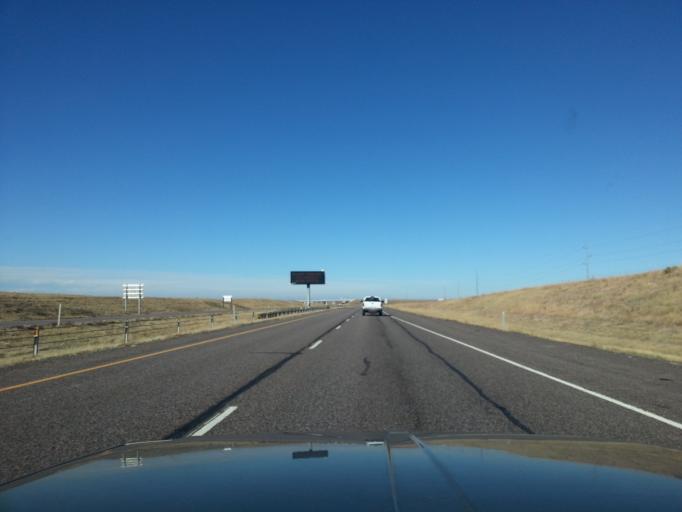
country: US
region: Colorado
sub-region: Adams County
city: Brighton
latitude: 39.8918
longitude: -104.7617
